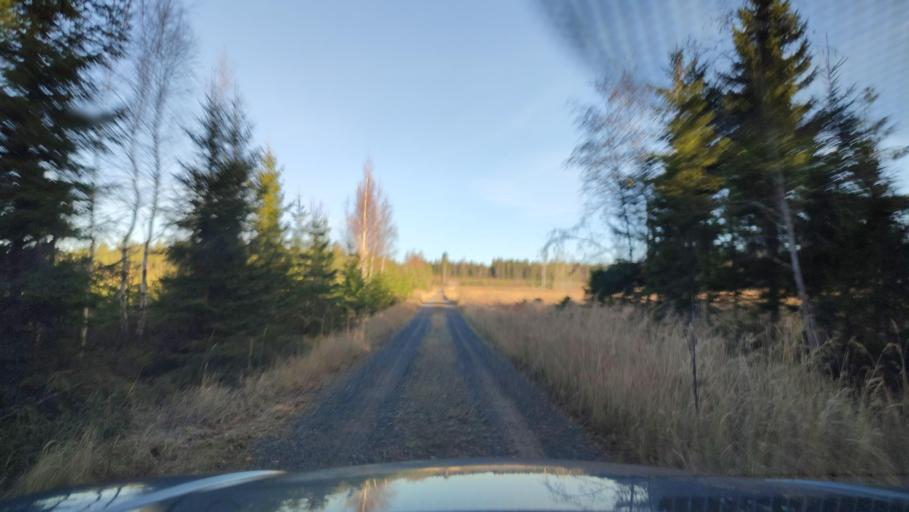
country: FI
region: Southern Ostrobothnia
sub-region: Suupohja
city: Karijoki
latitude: 62.1994
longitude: 21.6132
